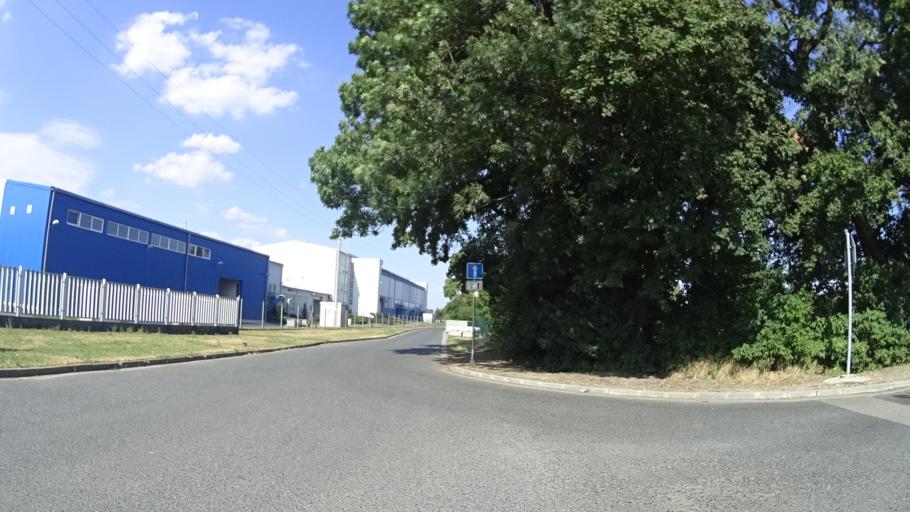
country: CZ
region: Zlin
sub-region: Okres Zlin
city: Ostrozska Nova Ves
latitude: 49.0034
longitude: 17.4302
